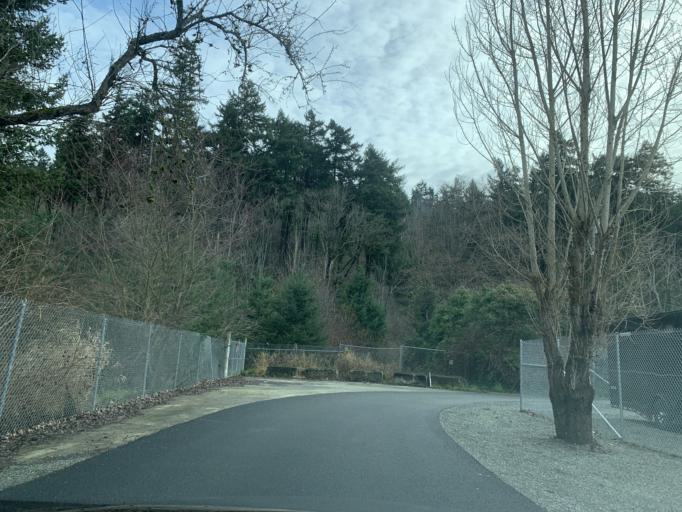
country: US
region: Washington
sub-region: Pierce County
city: Fife Heights
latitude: 47.2574
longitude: -122.3537
